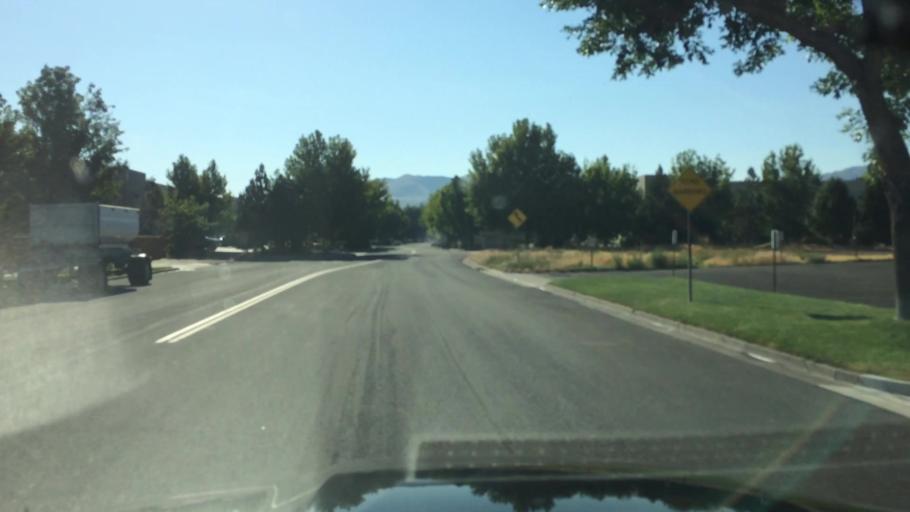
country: US
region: Nevada
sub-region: Washoe County
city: Sparks
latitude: 39.5090
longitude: -119.7627
